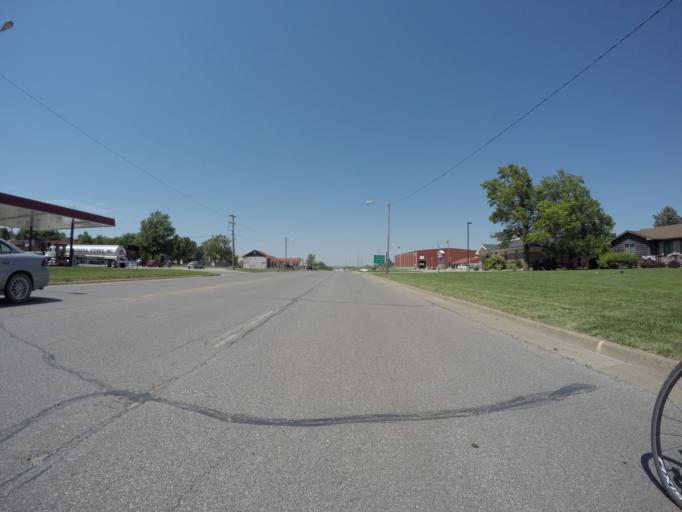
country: US
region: Kansas
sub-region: Nemaha County
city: Sabetha
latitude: 39.9025
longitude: -95.7882
